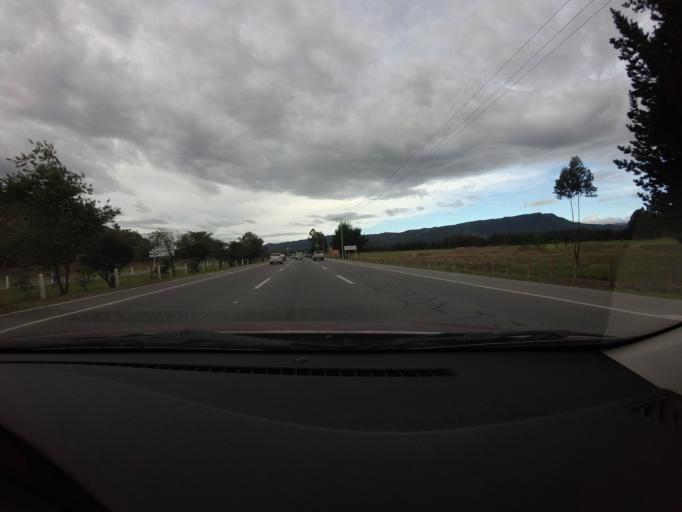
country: CO
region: Cundinamarca
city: Sopo
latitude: 4.9387
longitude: -73.9746
